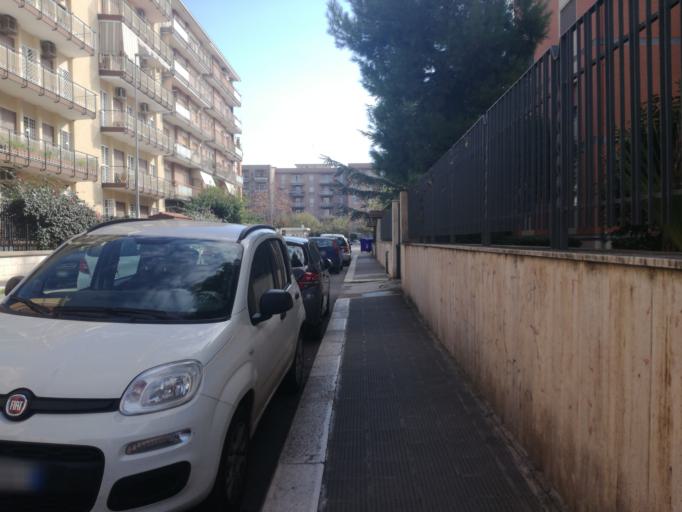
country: IT
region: Apulia
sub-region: Provincia di Bari
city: Bari
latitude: 41.1129
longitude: 16.8909
